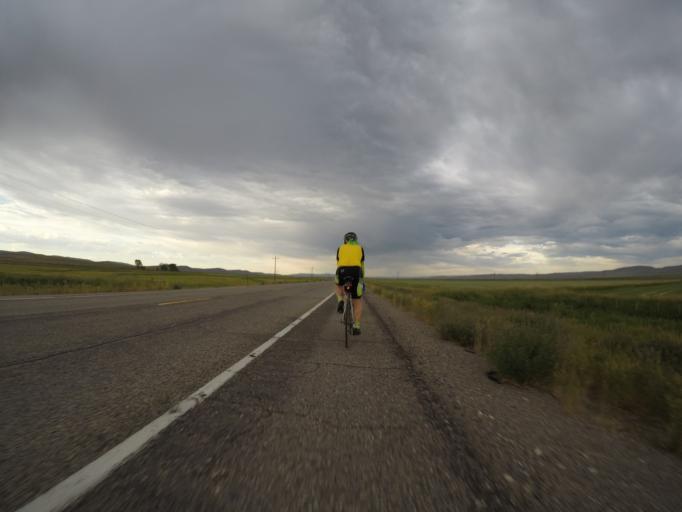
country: US
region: Utah
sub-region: Rich County
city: Randolph
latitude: 41.9512
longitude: -110.9505
